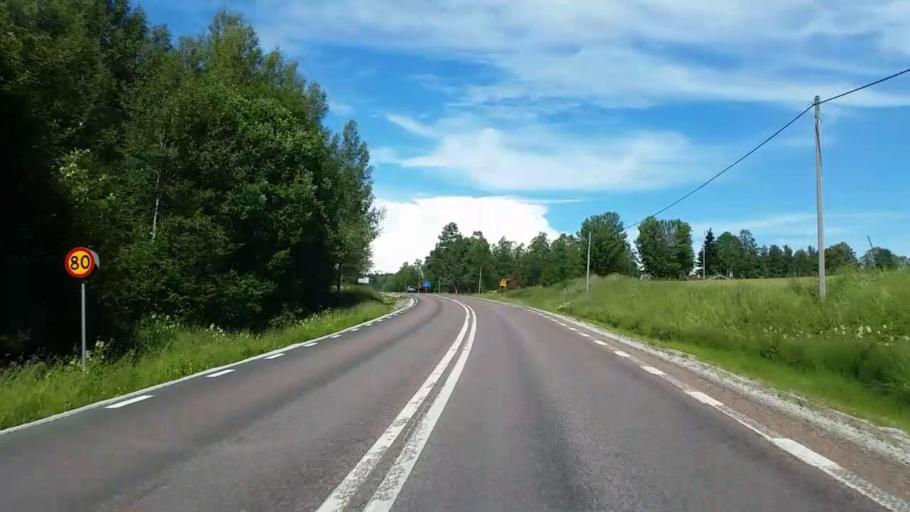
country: SE
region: Dalarna
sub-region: Rattviks Kommun
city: Raettvik
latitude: 61.0061
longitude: 15.2196
